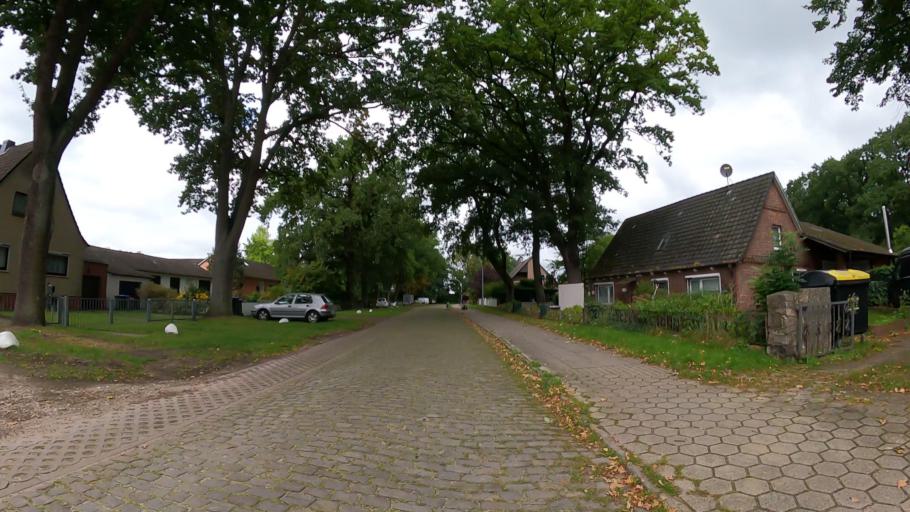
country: DE
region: Lower Saxony
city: Neu Wulmstorf
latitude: 53.4801
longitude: 9.8595
